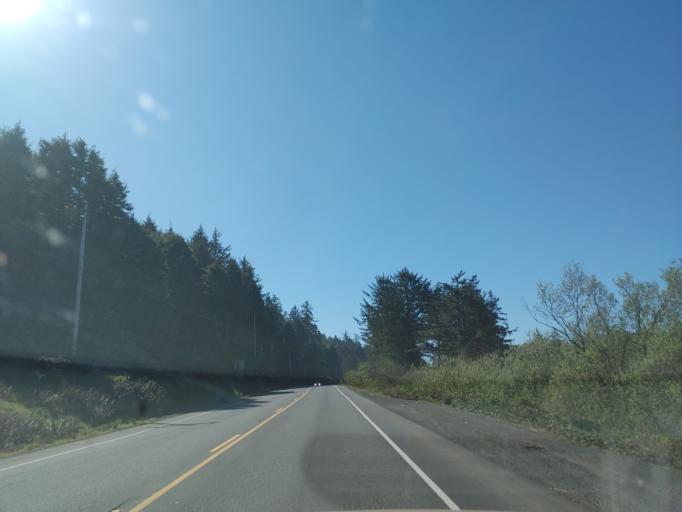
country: US
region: Oregon
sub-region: Tillamook County
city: Rockaway Beach
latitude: 45.5839
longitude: -123.9467
